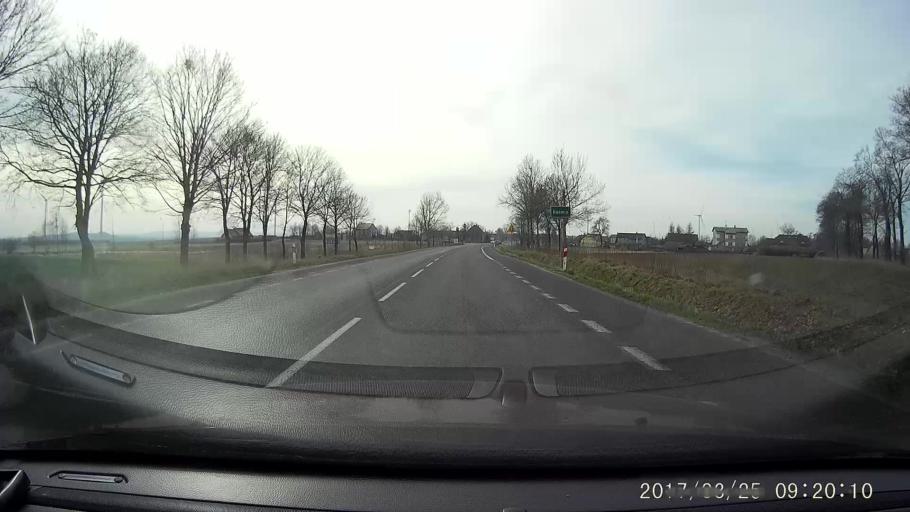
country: PL
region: Lower Silesian Voivodeship
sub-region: Powiat zgorzelecki
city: Sulikow
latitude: 51.0971
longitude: 15.0211
